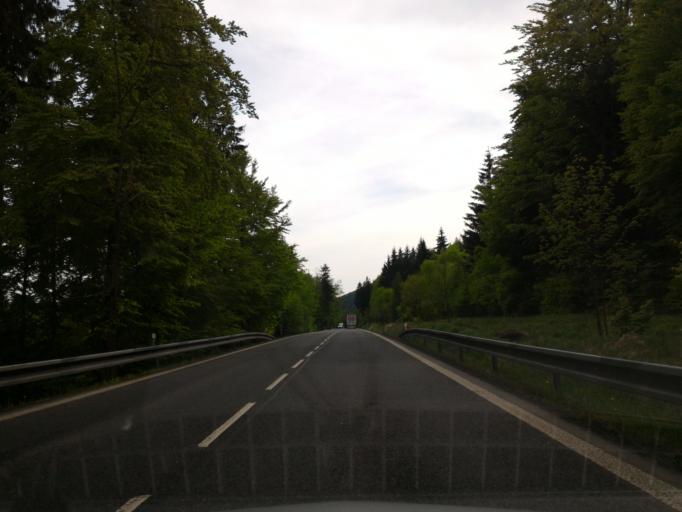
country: CZ
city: Cvikov
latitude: 50.8137
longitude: 14.5947
